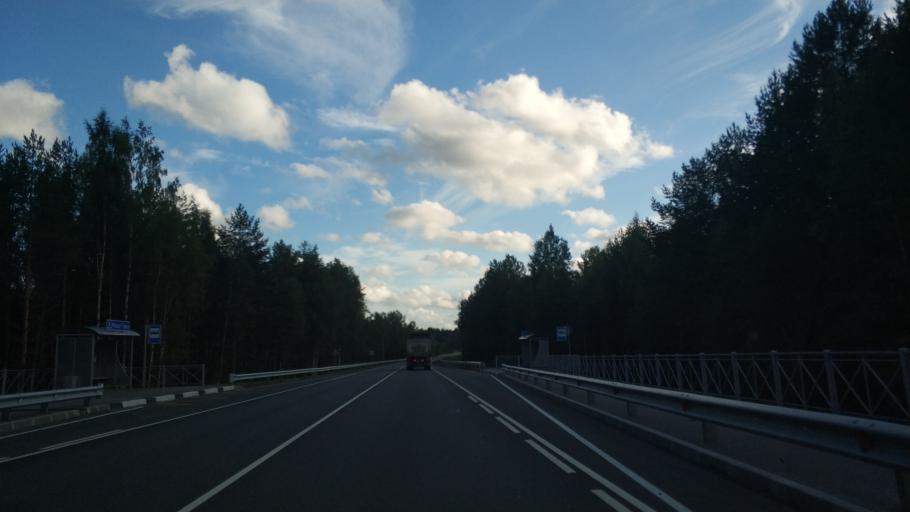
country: RU
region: Leningrad
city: Priozersk
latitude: 60.8658
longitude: 30.1595
